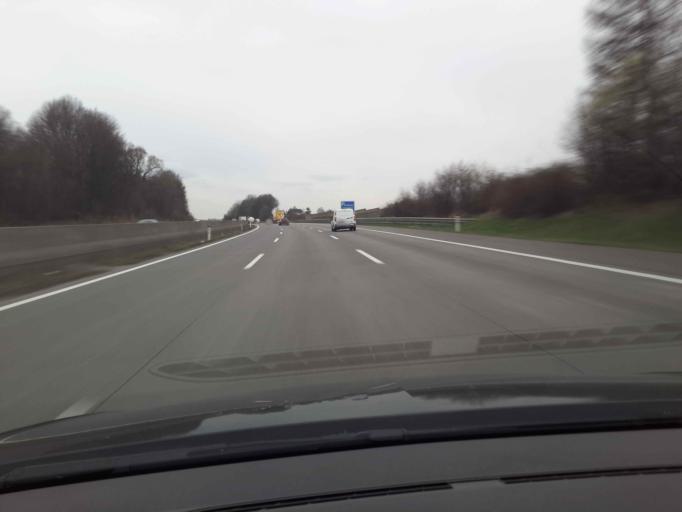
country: AT
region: Lower Austria
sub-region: Politischer Bezirk Amstetten
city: Amstetten
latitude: 48.1469
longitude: 14.9078
